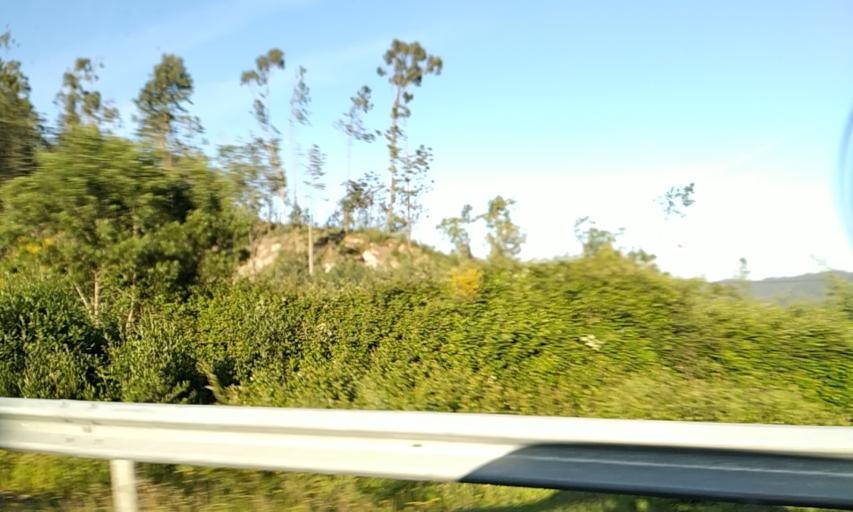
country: PT
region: Braga
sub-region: Braga
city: Oliveira
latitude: 41.4504
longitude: -8.4900
